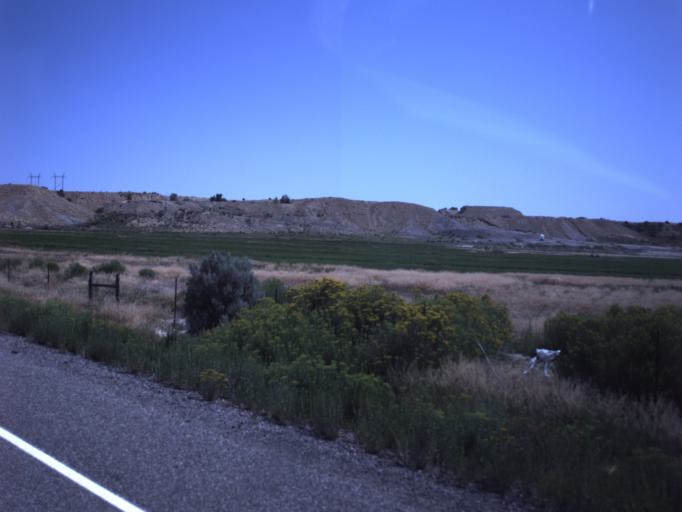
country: US
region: Utah
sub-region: Emery County
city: Ferron
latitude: 38.8786
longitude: -111.2893
